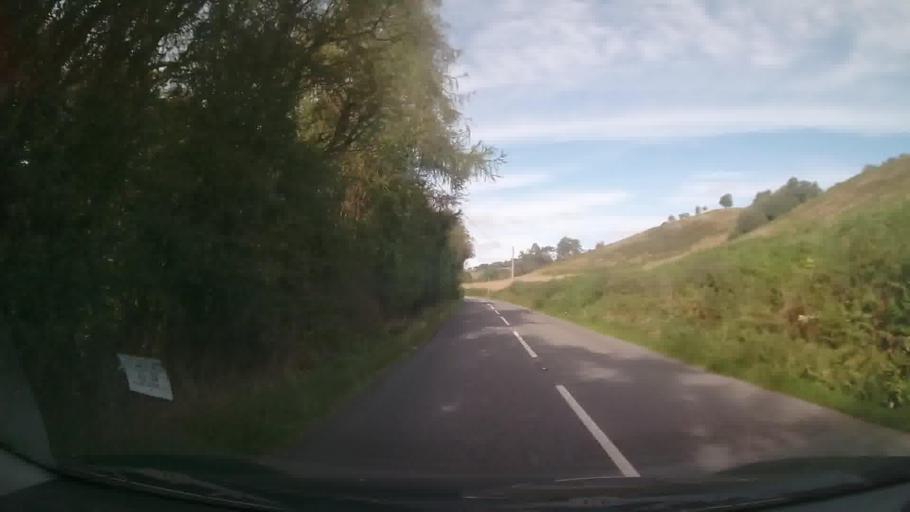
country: GB
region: England
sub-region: Shropshire
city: Lydham
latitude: 52.5622
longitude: -2.9980
